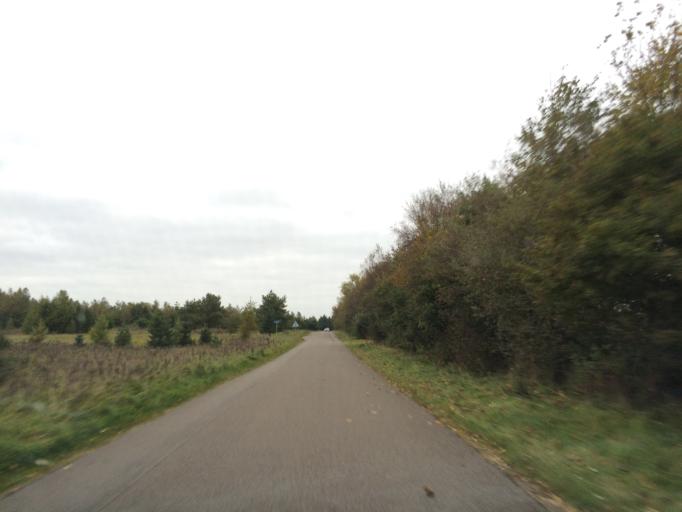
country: DK
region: Central Jutland
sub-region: Holstebro Kommune
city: Ulfborg
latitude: 56.2246
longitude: 8.4345
